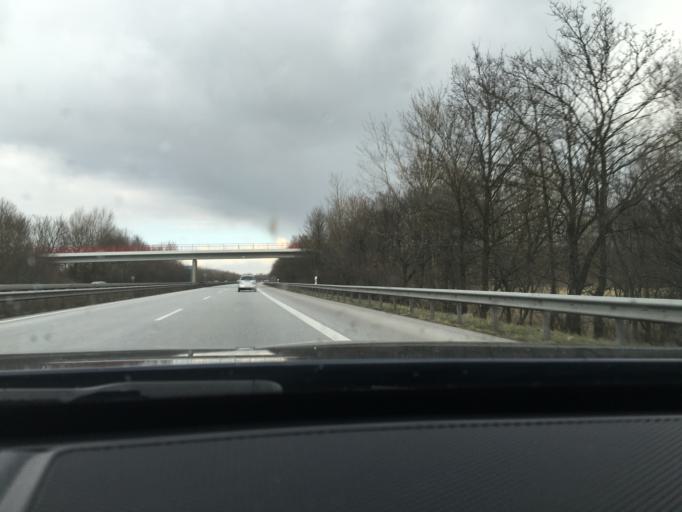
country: DE
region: Lower Saxony
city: Loxstedt
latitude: 53.4483
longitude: 8.5866
